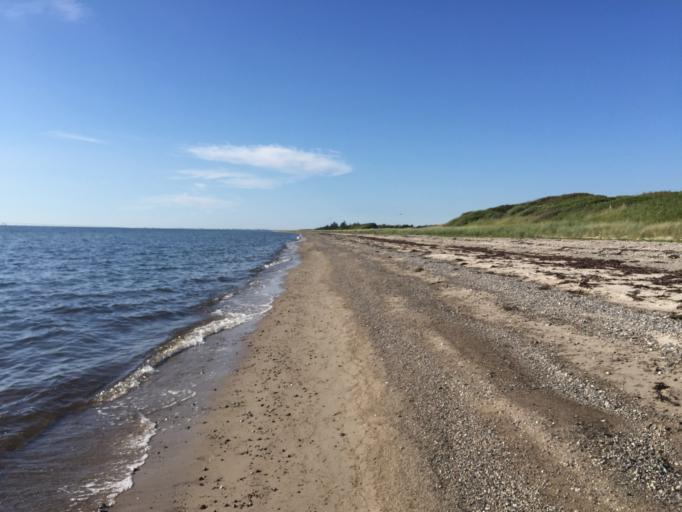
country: DK
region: Zealand
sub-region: Slagelse Kommune
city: Korsor
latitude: 55.2235
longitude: 11.1719
